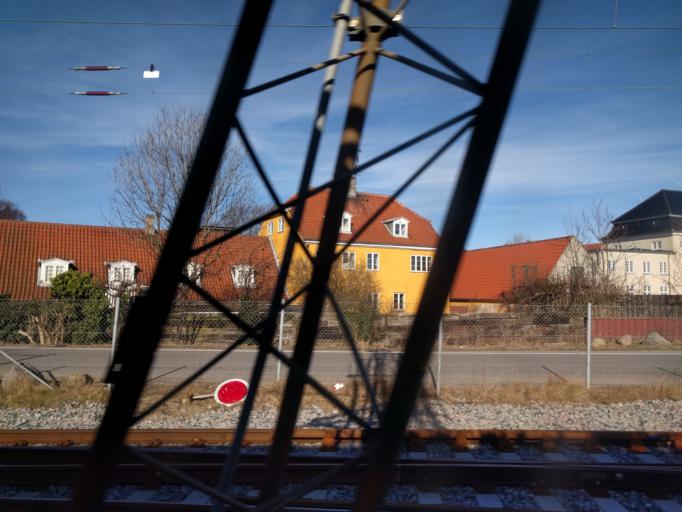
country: DK
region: Capital Region
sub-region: Helsingor Kommune
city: Helsingor
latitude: 56.0272
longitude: 12.6066
